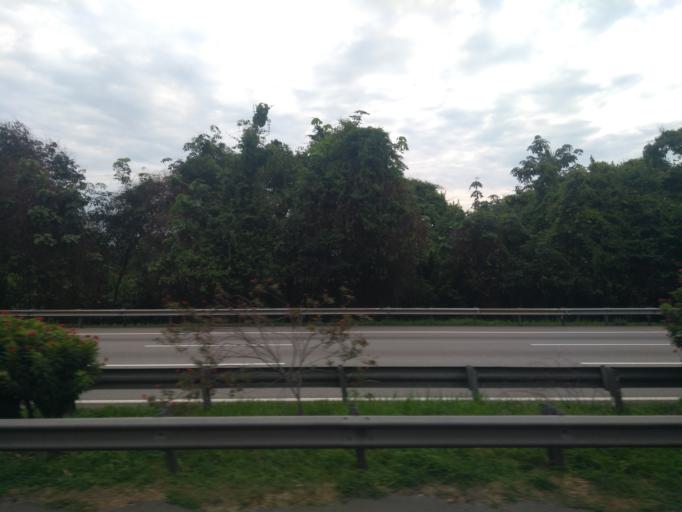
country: MY
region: Melaka
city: Alor Gajah
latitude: 2.3831
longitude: 102.2307
